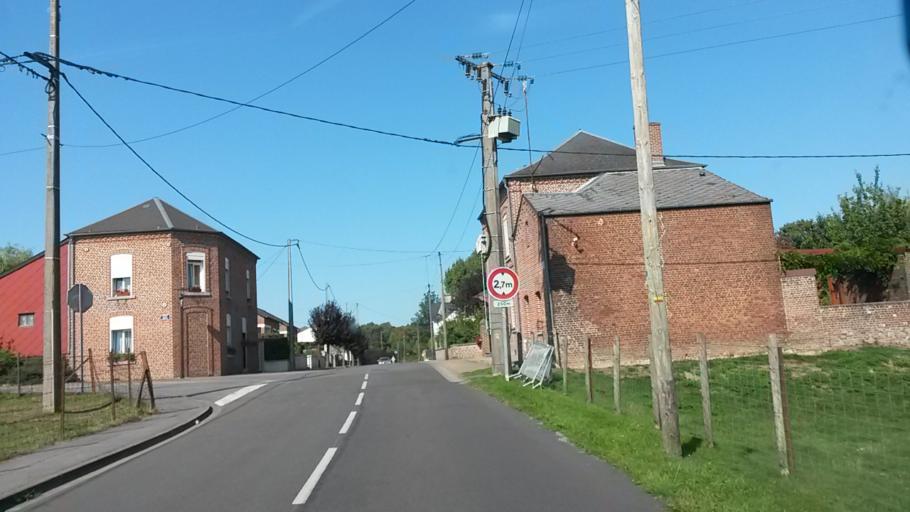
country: FR
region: Nord-Pas-de-Calais
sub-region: Departement du Nord
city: Avesnelles
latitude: 50.1224
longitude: 3.9429
